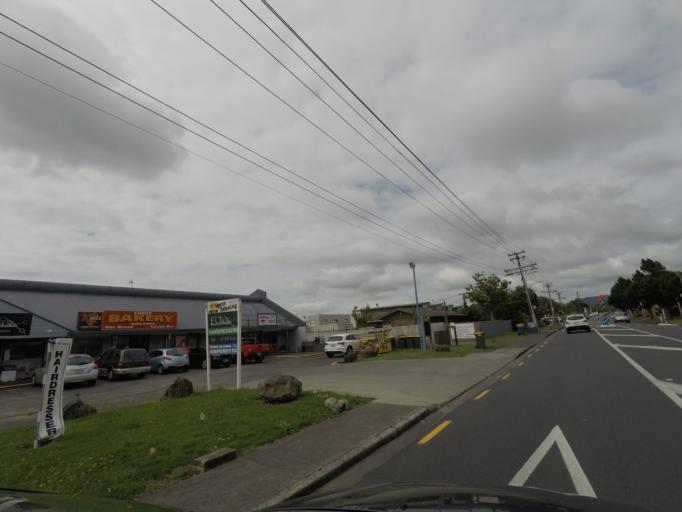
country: NZ
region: Auckland
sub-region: Auckland
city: Waitakere
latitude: -36.8954
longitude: 174.6276
